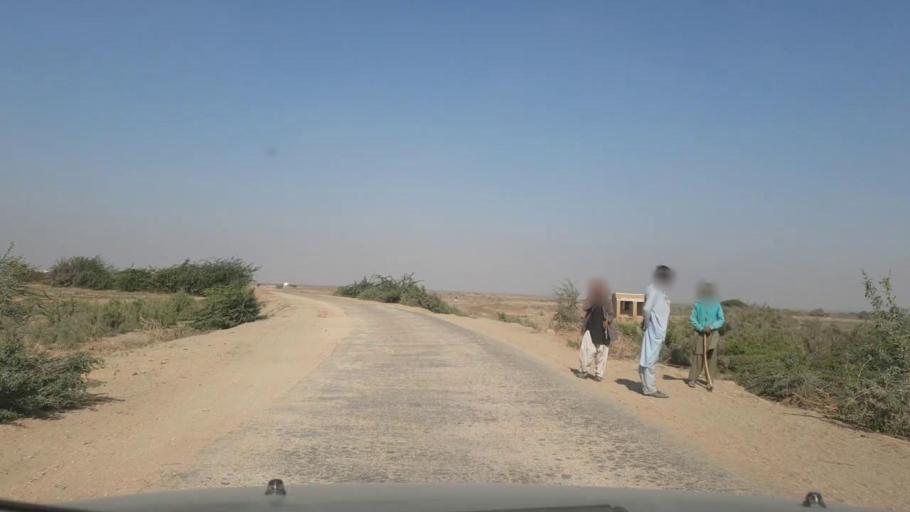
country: PK
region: Sindh
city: Thatta
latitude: 24.8111
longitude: 67.8995
